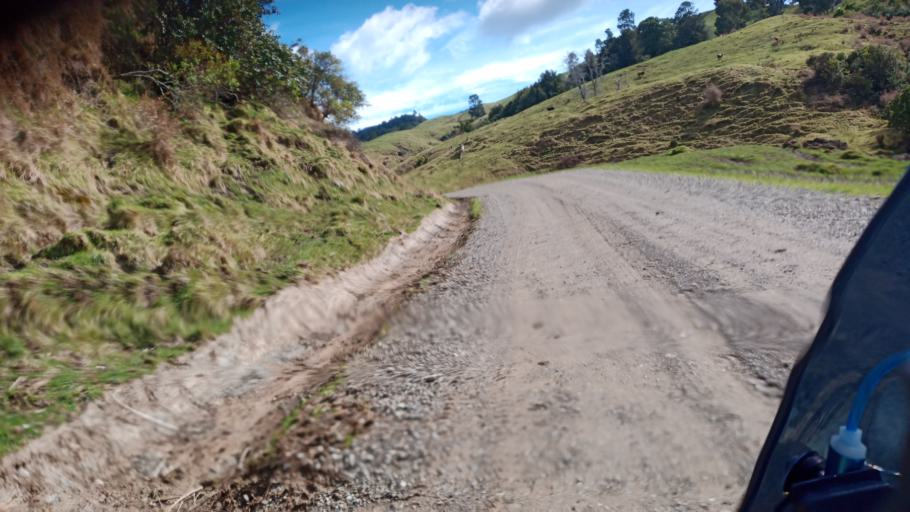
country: NZ
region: Hawke's Bay
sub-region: Wairoa District
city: Wairoa
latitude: -38.7352
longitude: 177.2977
